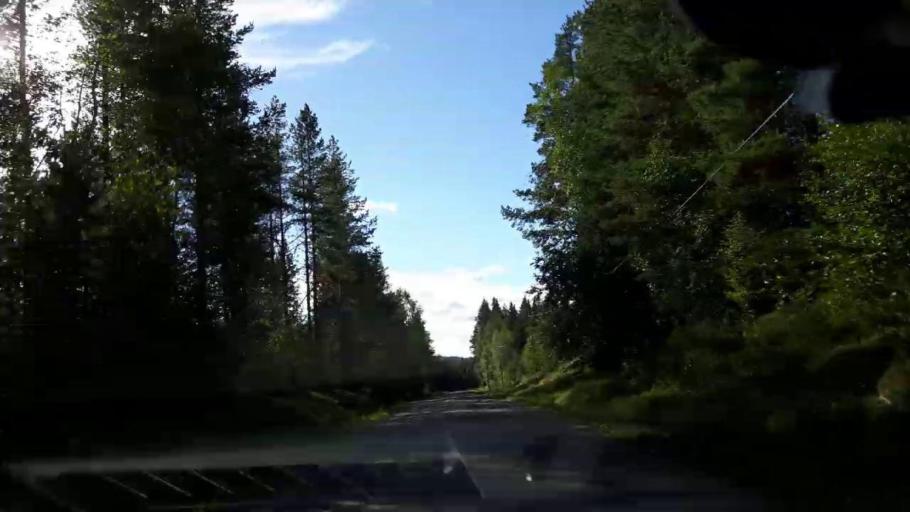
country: SE
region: Jaemtland
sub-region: Ragunda Kommun
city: Hammarstrand
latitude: 63.4799
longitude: 16.1436
